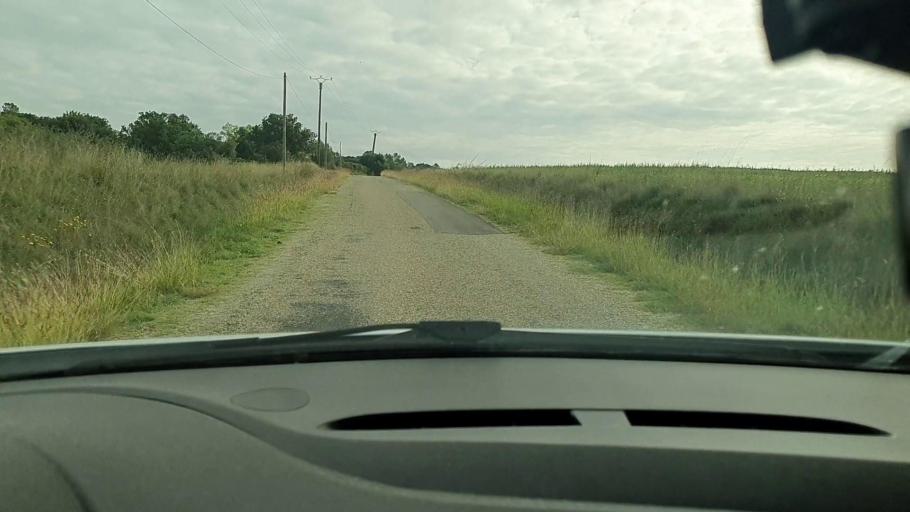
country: FR
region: Languedoc-Roussillon
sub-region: Departement du Gard
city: Montaren-et-Saint-Mediers
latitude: 44.0900
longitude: 4.3390
